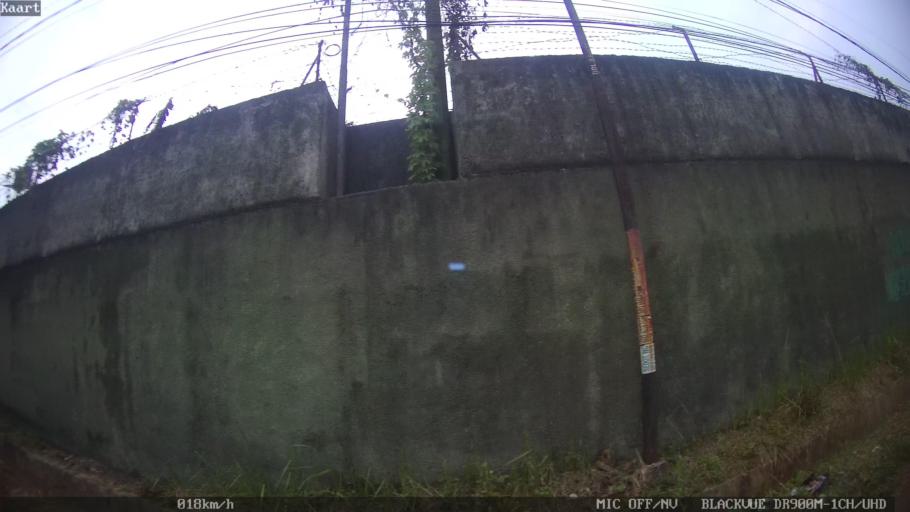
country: ID
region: Lampung
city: Kedaton
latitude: -5.4034
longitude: 105.2697
